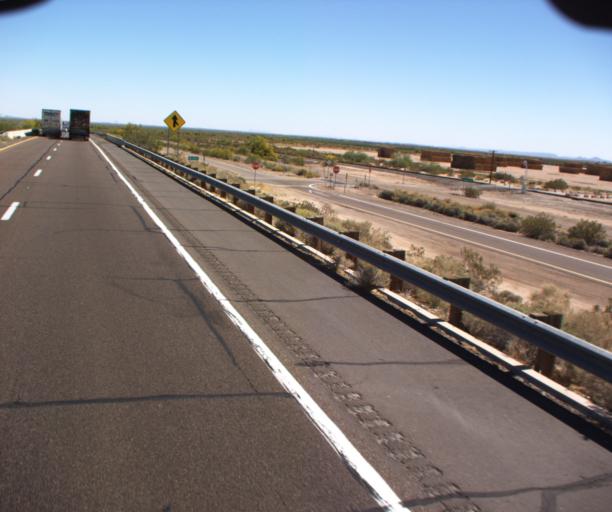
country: US
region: Arizona
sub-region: Yuma County
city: Wellton
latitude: 32.8244
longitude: -113.4431
